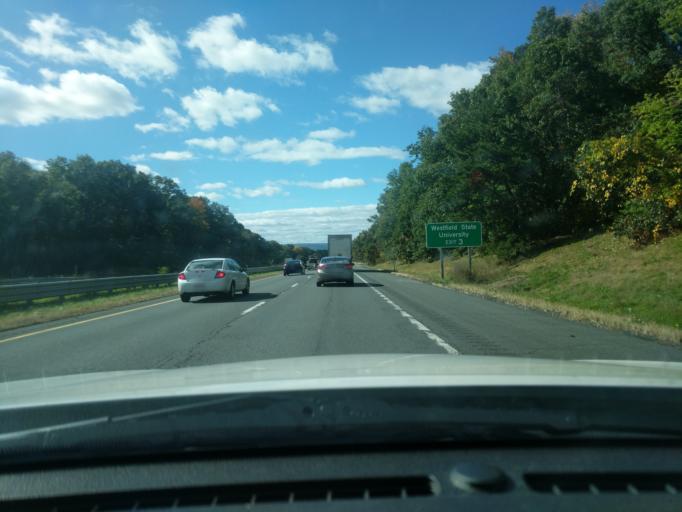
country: US
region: Massachusetts
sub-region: Hampden County
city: Westfield
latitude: 42.1391
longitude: -72.6958
